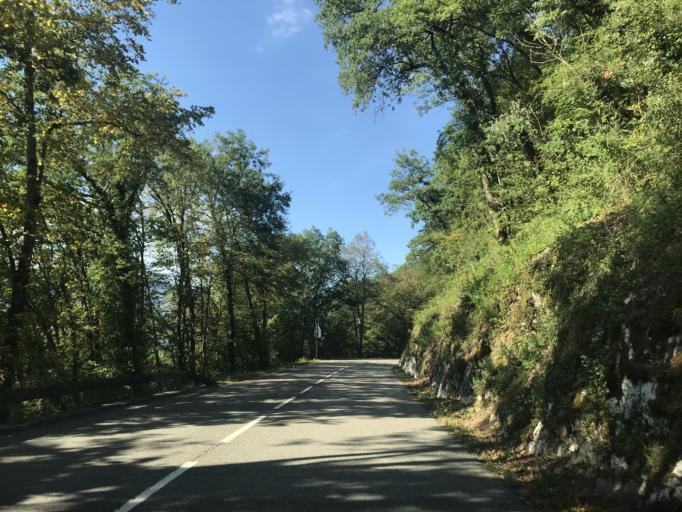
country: FR
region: Rhone-Alpes
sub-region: Departement de l'Ain
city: Culoz
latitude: 45.7975
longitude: 5.7862
